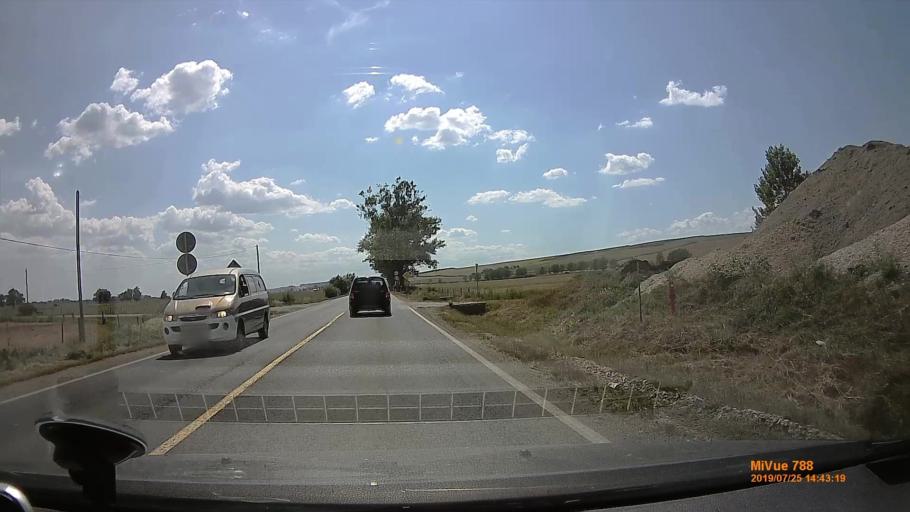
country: HU
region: Borsod-Abauj-Zemplen
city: Halmaj
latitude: 48.2740
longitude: 21.0127
